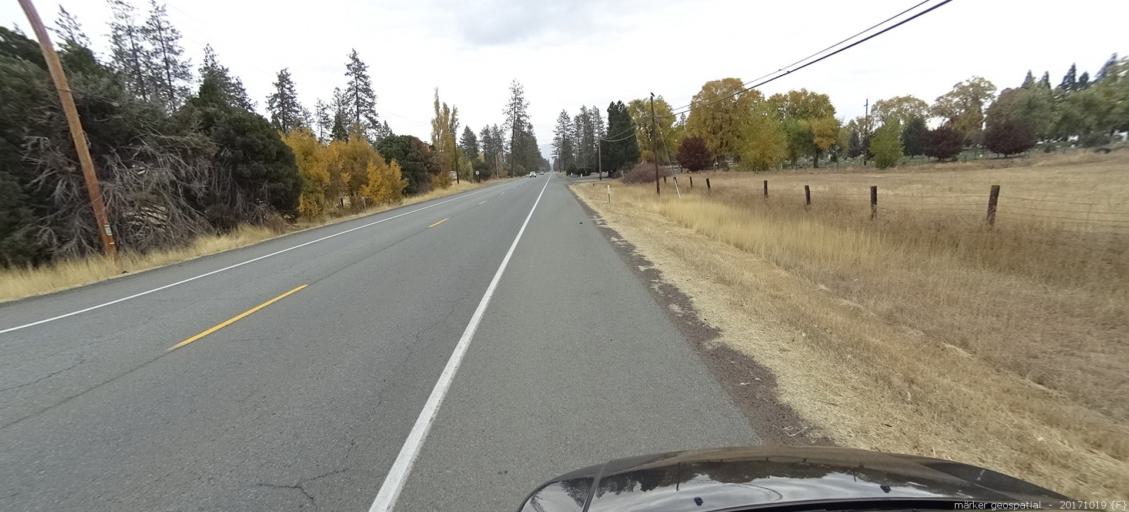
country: US
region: California
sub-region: Shasta County
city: Burney
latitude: 41.0557
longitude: -121.3857
